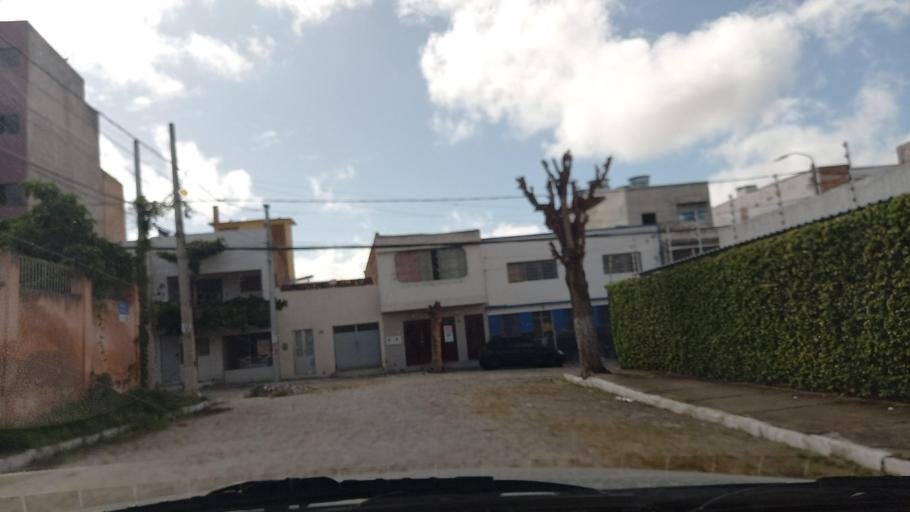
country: BR
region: Pernambuco
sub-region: Caruaru
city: Caruaru
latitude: -8.2895
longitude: -35.9797
